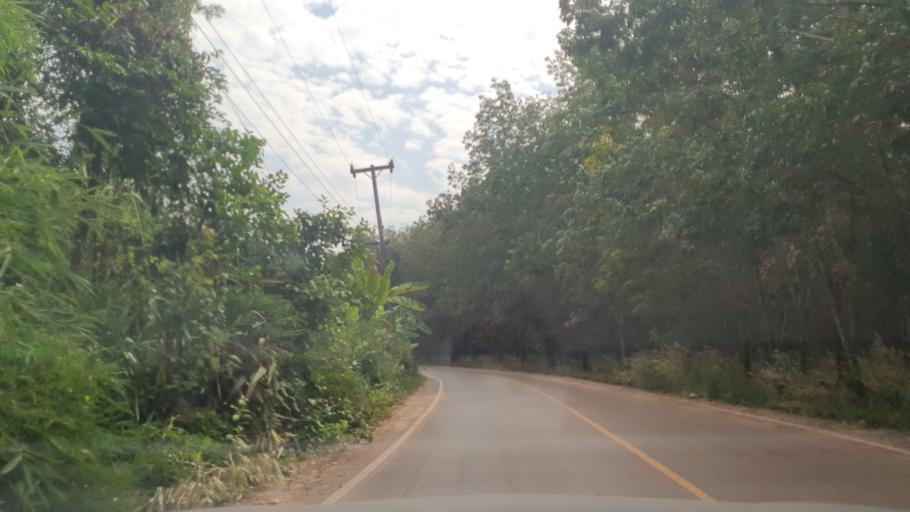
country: TH
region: Changwat Bueng Kan
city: Si Wilai
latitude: 18.2795
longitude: 103.7933
